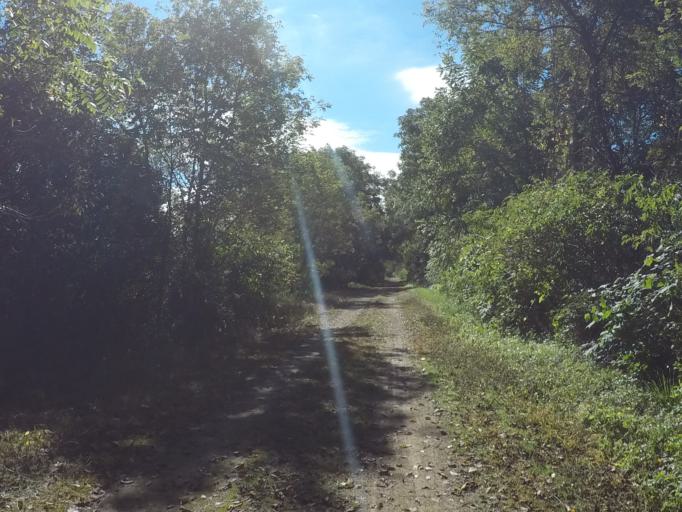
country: US
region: Wisconsin
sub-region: Richland County
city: Richland Center
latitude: 43.2904
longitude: -90.3251
